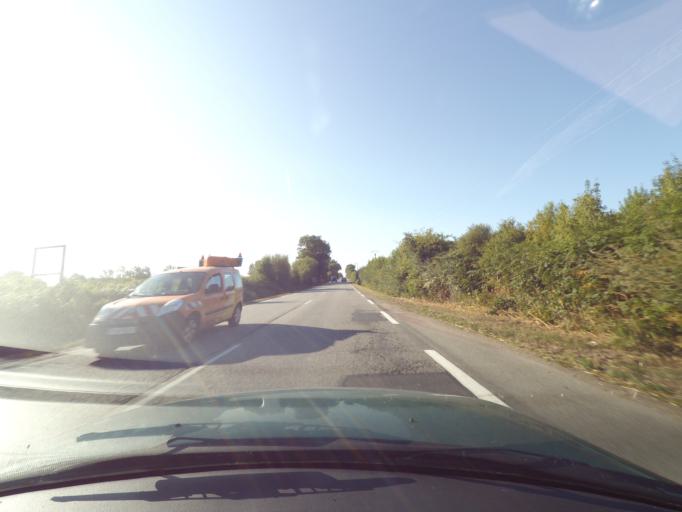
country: FR
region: Poitou-Charentes
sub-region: Departement des Deux-Sevres
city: Viennay
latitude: 46.6953
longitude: -0.2763
